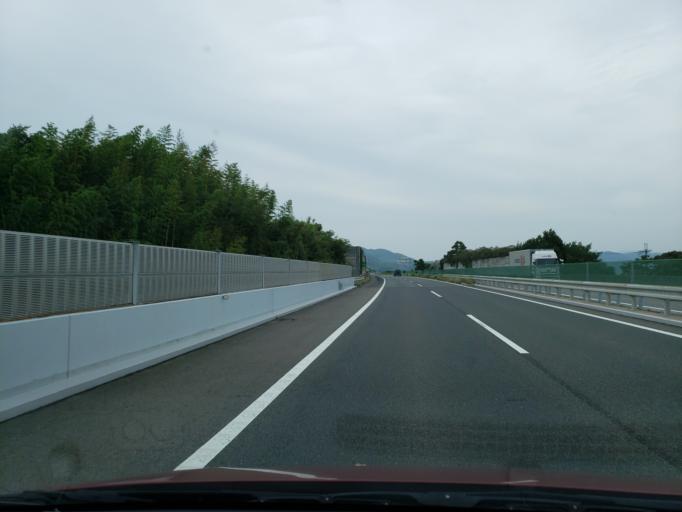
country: JP
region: Hyogo
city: Sumoto
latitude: 34.3773
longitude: 134.8611
